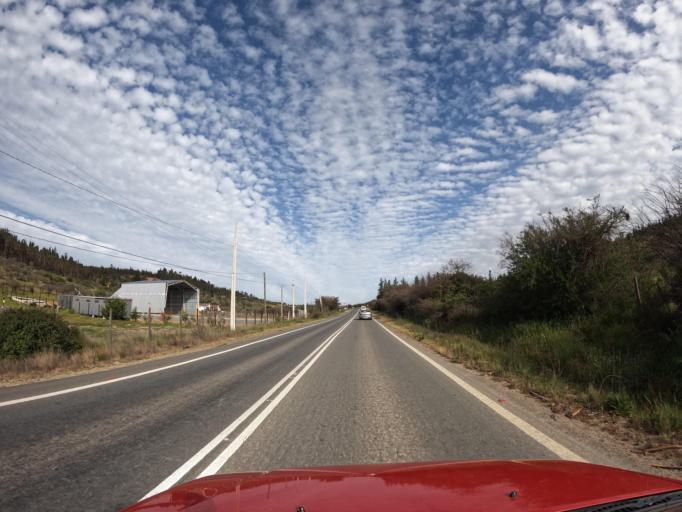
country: CL
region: O'Higgins
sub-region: Provincia de Colchagua
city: Santa Cruz
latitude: -34.3099
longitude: -71.7769
